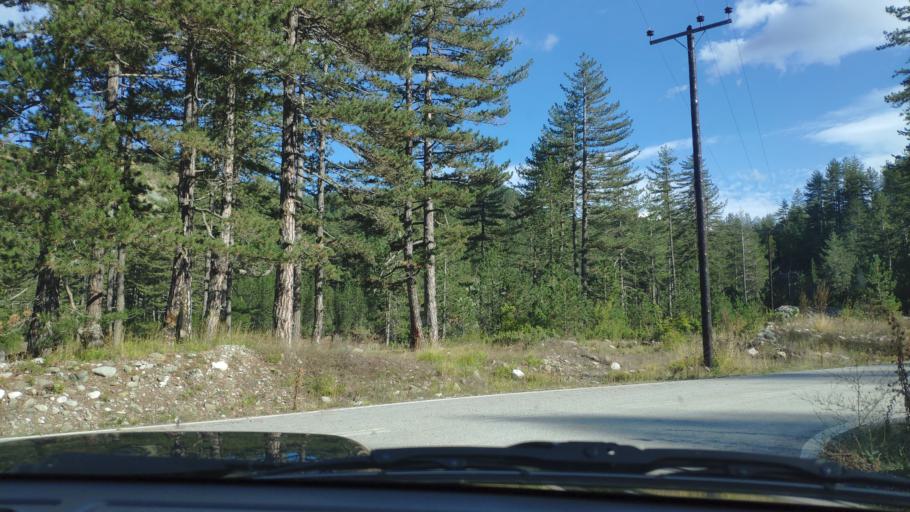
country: AL
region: Korce
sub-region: Rrethi i Devollit
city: Miras
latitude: 40.4113
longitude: 20.8737
